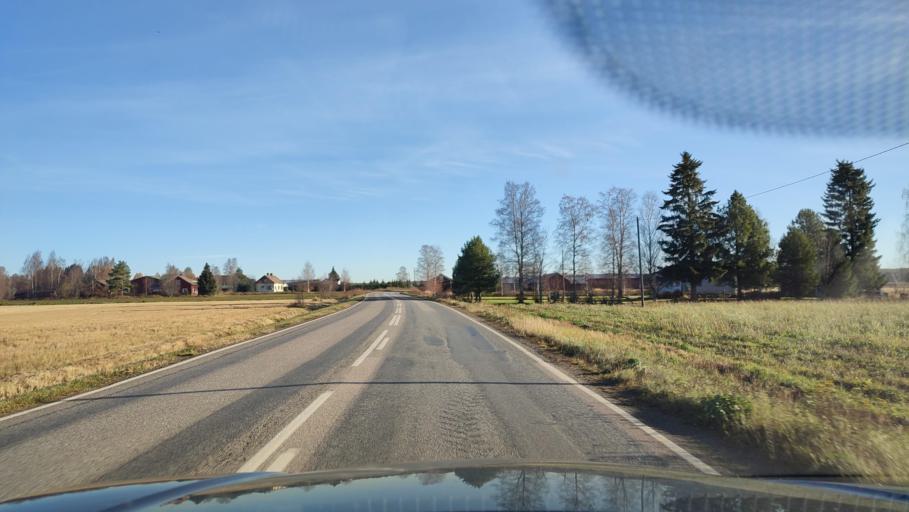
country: FI
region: Southern Ostrobothnia
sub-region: Suupohja
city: Karijoki
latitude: 62.2340
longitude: 21.6570
